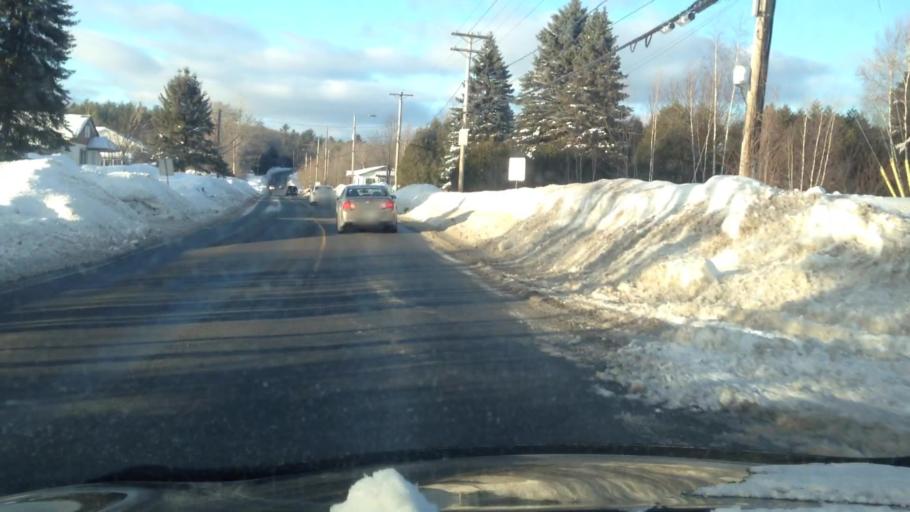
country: CA
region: Quebec
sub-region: Laurentides
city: Saint-Jerome
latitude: 45.8010
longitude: -73.9844
